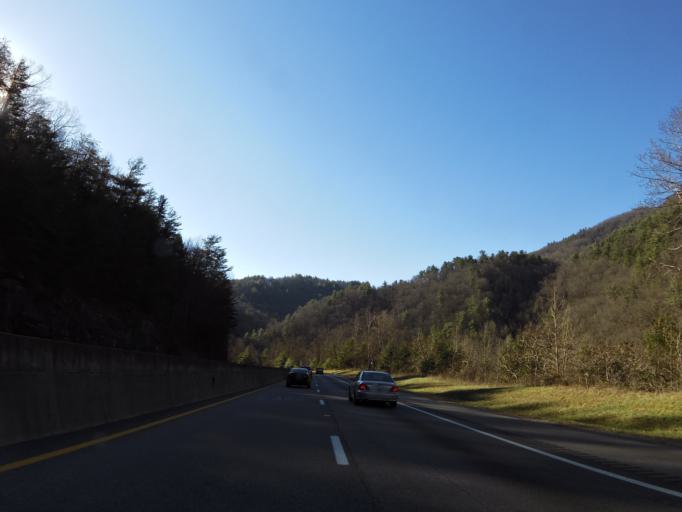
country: US
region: North Carolina
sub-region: Haywood County
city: Cove Creek
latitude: 35.7441
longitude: -83.0358
